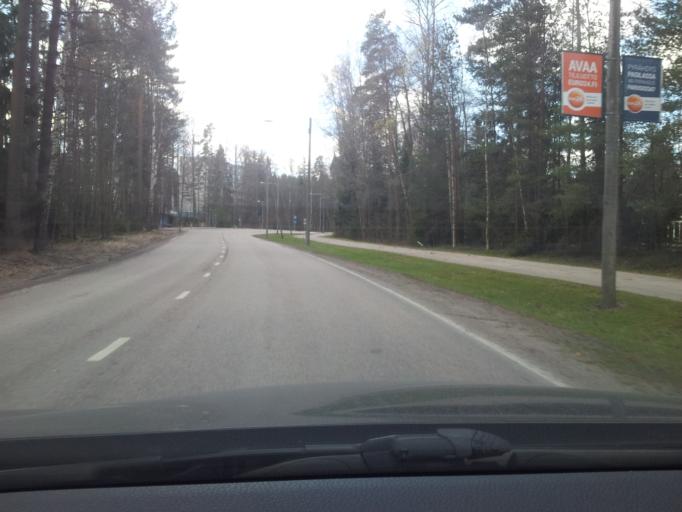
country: FI
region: Uusimaa
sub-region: Helsinki
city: Espoo
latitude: 60.1511
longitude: 24.6922
